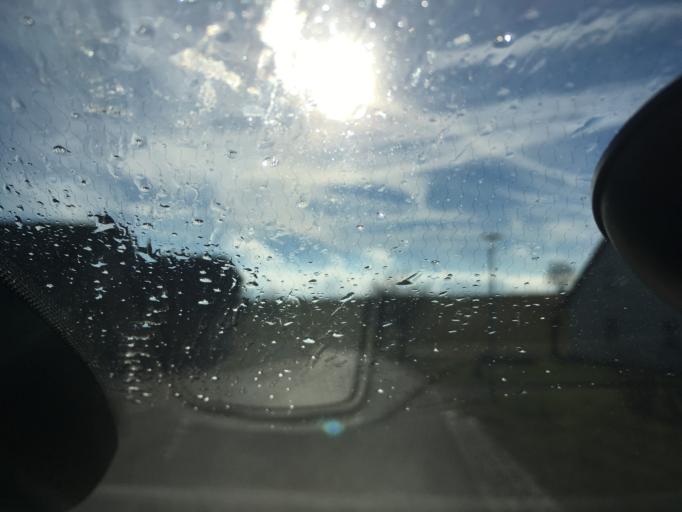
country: DE
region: Baden-Wuerttemberg
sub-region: Freiburg Region
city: Gorwihl
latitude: 47.6405
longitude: 8.0802
